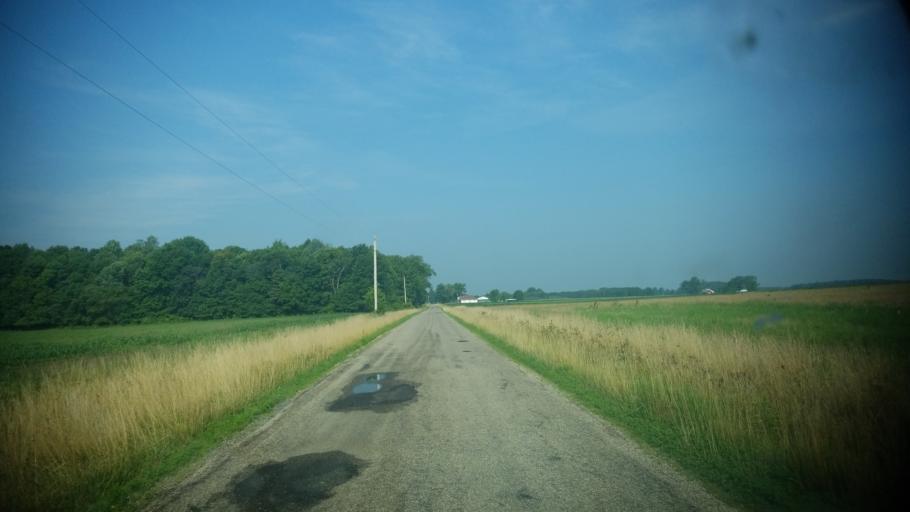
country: US
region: Illinois
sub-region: Clay County
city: Flora
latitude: 38.6031
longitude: -88.4294
